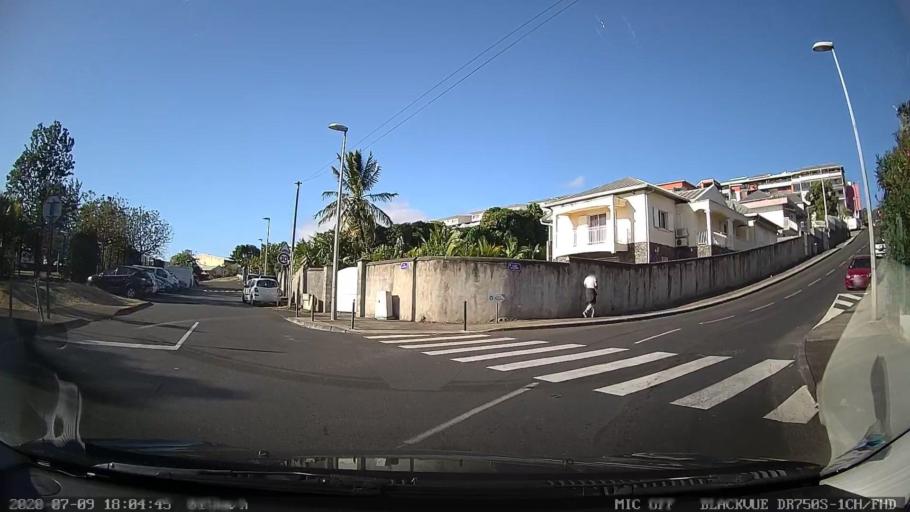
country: RE
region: Reunion
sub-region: Reunion
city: Saint-Denis
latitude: -20.8985
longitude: 55.4723
